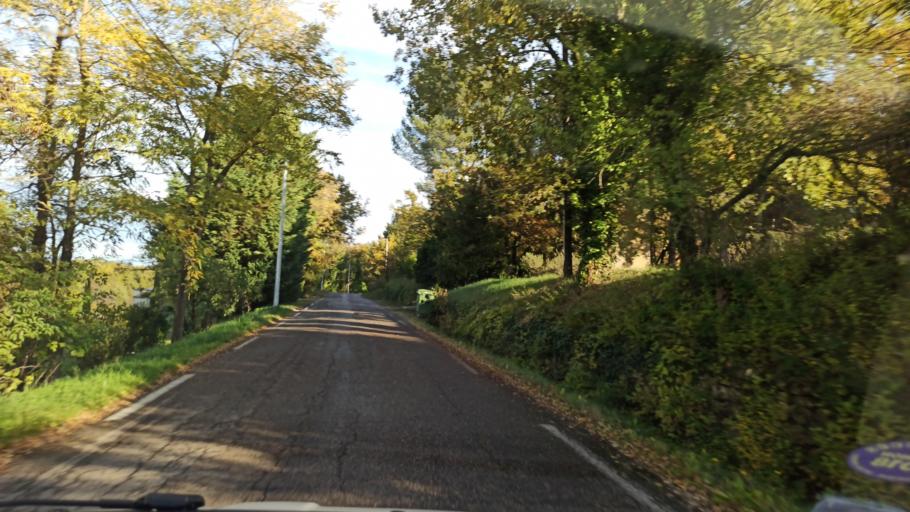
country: FR
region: Provence-Alpes-Cote d'Azur
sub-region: Departement du Vaucluse
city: Goult
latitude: 43.8374
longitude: 5.2633
